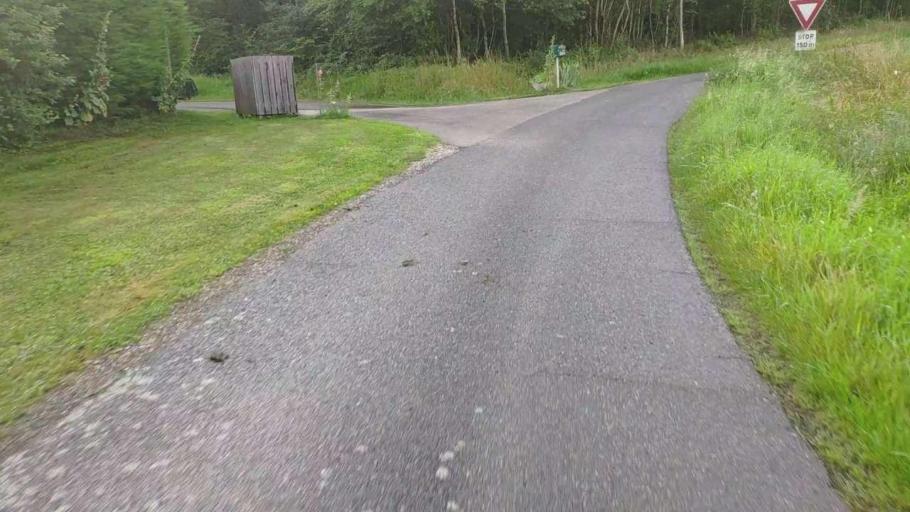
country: FR
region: Franche-Comte
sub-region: Departement du Jura
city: Bletterans
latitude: 46.8631
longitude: 5.5275
